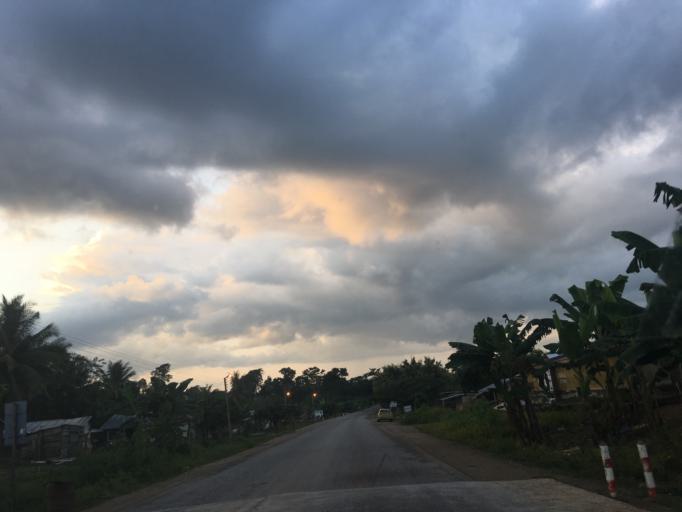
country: GH
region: Western
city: Bibiani
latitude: 6.7492
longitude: -2.5044
